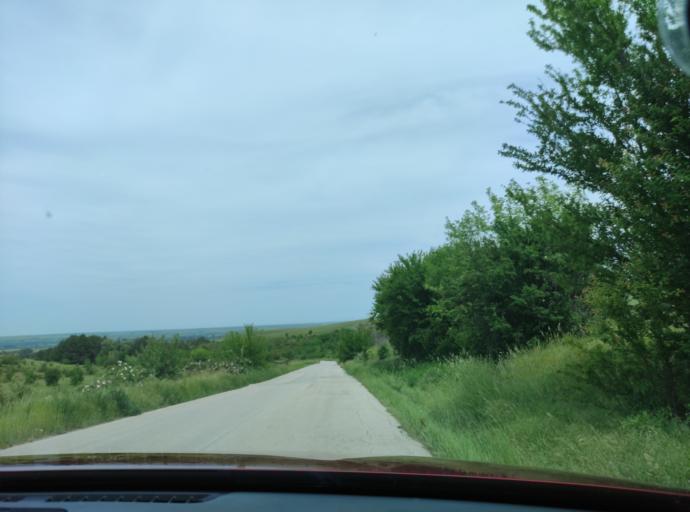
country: BG
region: Pleven
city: Iskur
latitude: 43.5323
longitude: 24.3026
